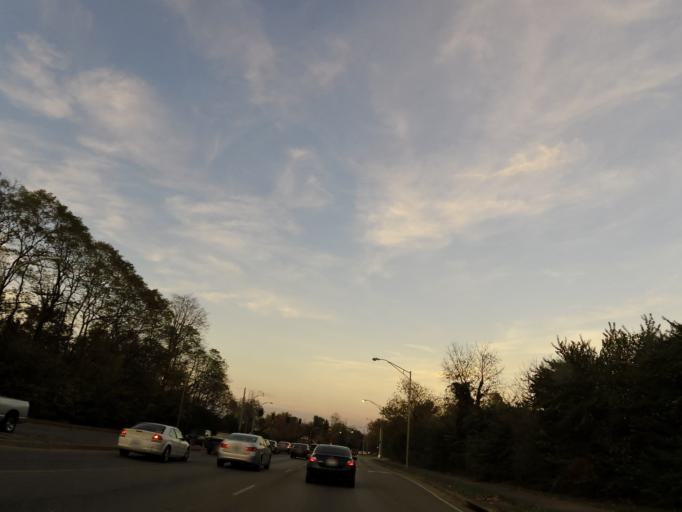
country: US
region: Kentucky
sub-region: Fayette County
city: Lexington
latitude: 37.9892
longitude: -84.4575
